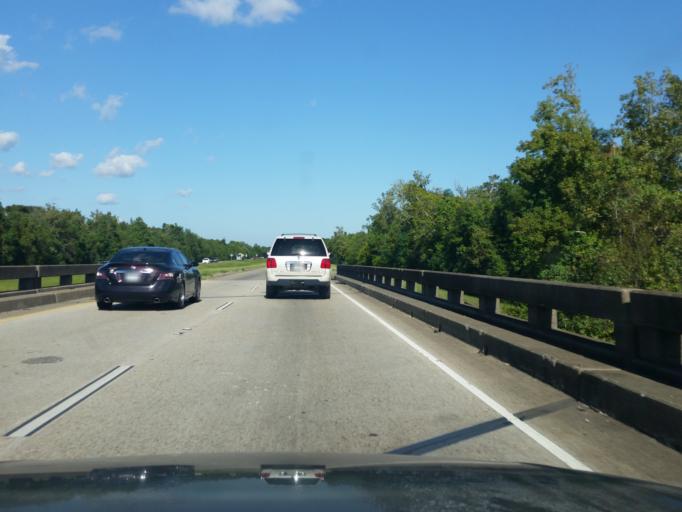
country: US
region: Mississippi
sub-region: Hancock County
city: Pearlington
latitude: 30.2983
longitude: -89.6631
